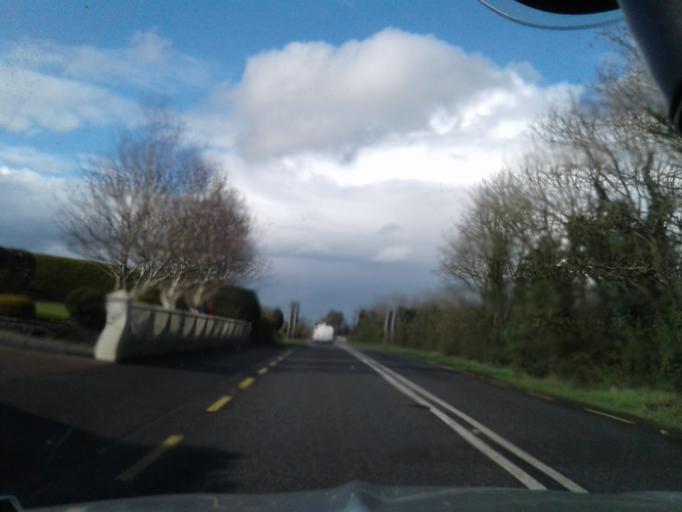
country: IE
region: Ulster
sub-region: County Monaghan
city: Monaghan
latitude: 54.3475
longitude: -6.9629
